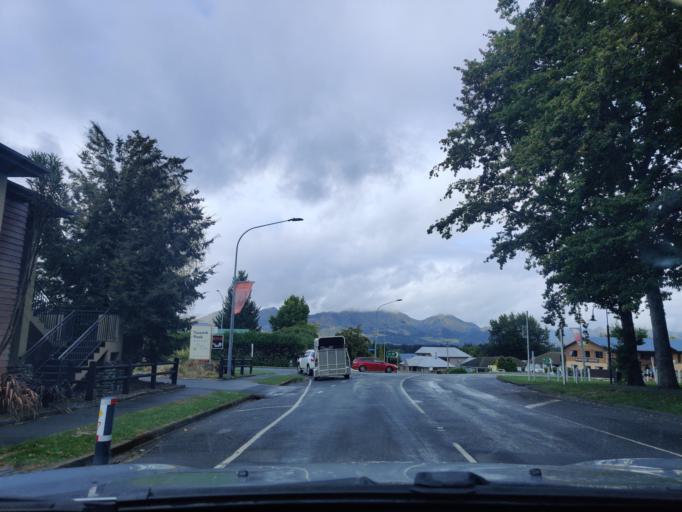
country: NZ
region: Canterbury
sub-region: Hurunui District
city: Amberley
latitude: -42.5250
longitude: 172.8292
